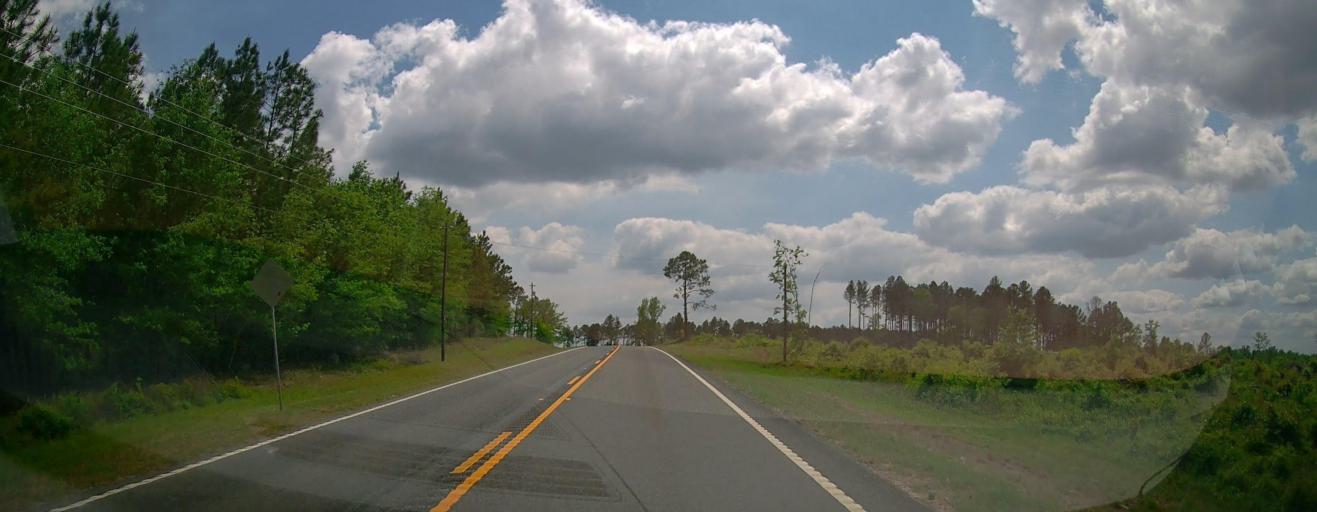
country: US
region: Georgia
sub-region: Treutlen County
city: Soperton
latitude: 32.4153
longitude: -82.6085
